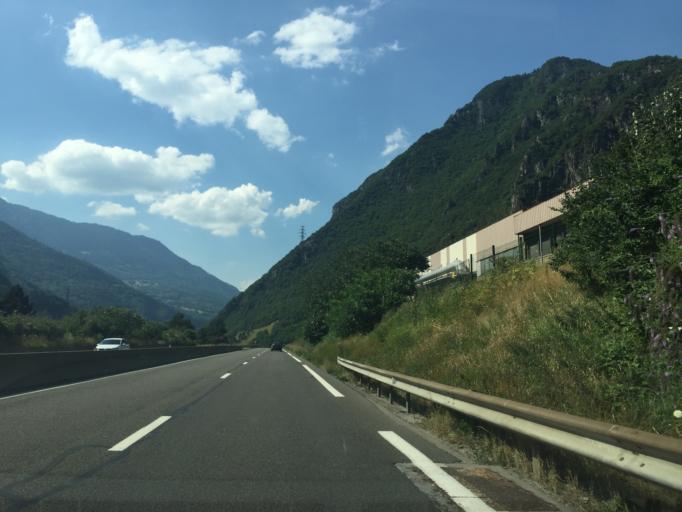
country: FR
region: Rhone-Alpes
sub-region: Departement de la Savoie
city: Aigueblanche
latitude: 45.5228
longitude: 6.4837
